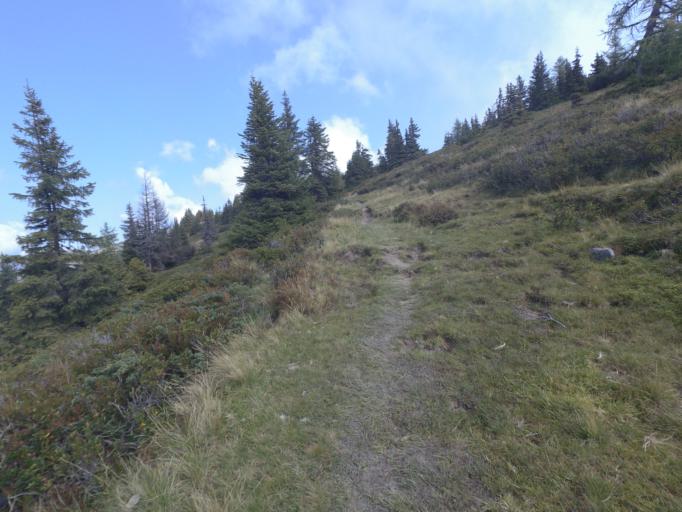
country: AT
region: Salzburg
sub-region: Politischer Bezirk Sankt Johann im Pongau
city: Kleinarl
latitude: 47.2645
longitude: 13.2773
